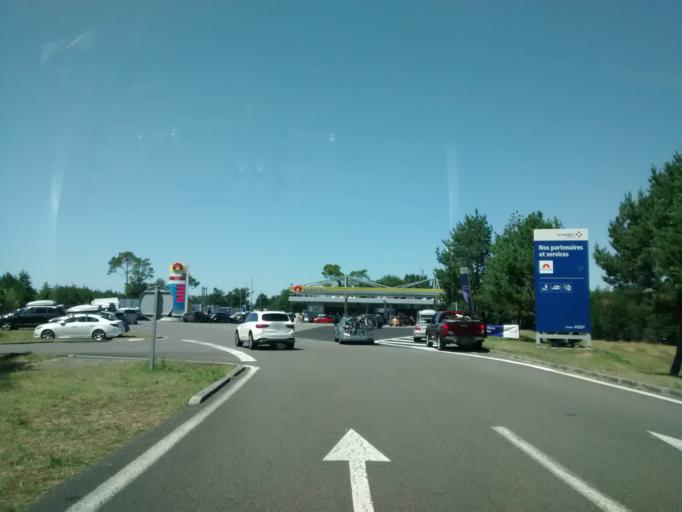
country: FR
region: Aquitaine
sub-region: Departement de la Dordogne
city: Le Pizou
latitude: 45.0007
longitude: 0.0378
